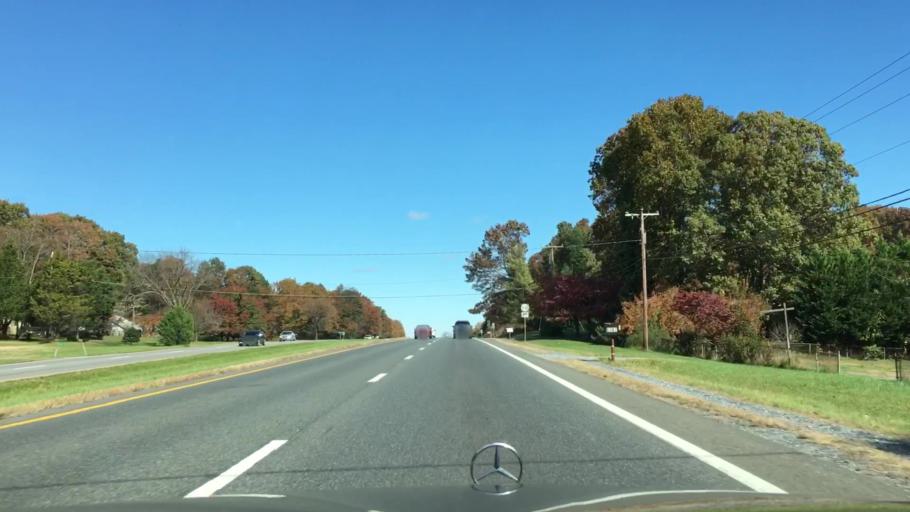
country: US
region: Virginia
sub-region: Campbell County
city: Rustburg
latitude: 37.2185
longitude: -79.1939
